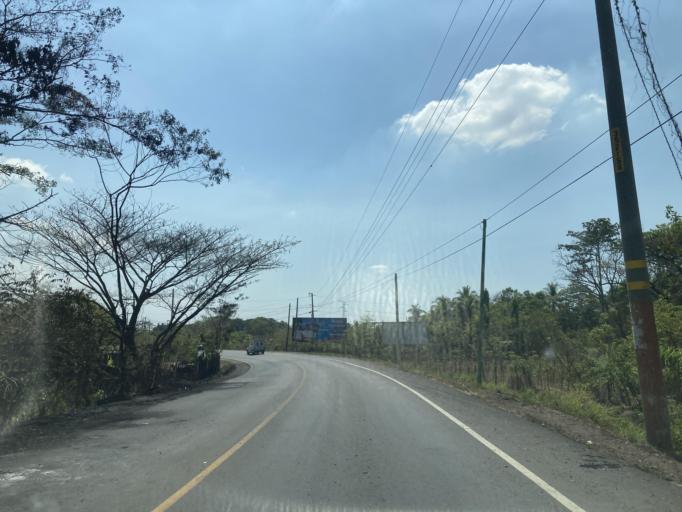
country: GT
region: Escuintla
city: Guanagazapa
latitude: 14.2016
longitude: -90.7126
